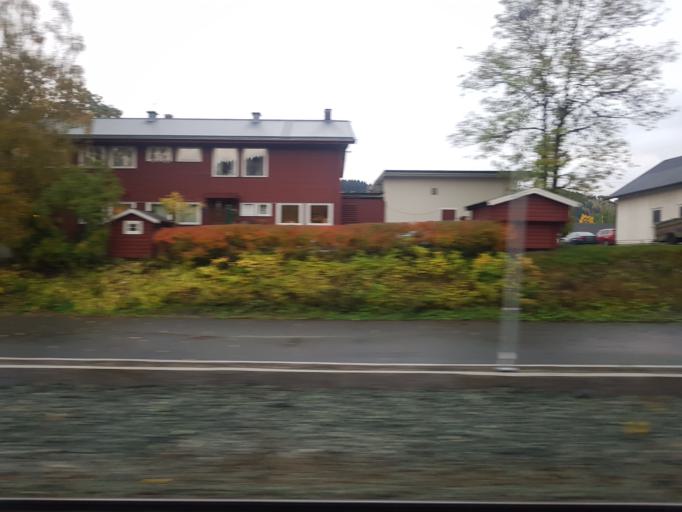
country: NO
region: Sor-Trondelag
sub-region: Melhus
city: Lundamo
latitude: 63.1356
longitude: 10.2603
